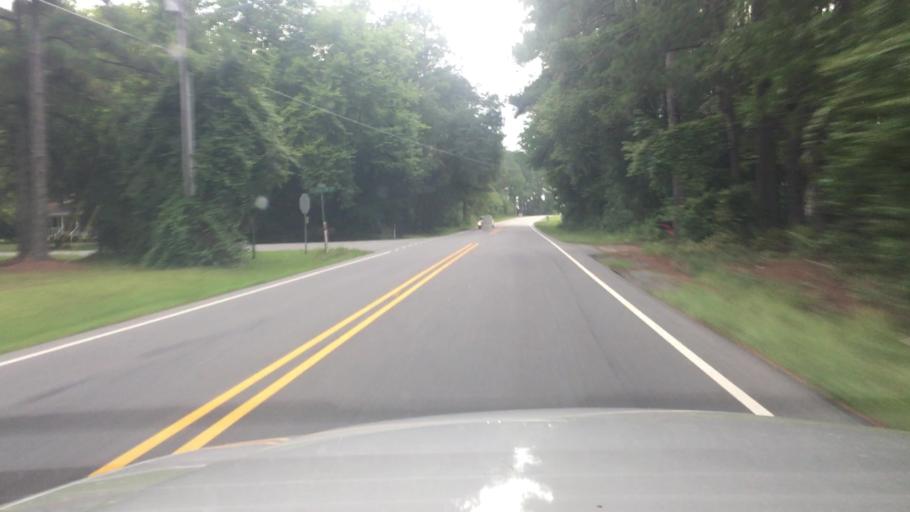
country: US
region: North Carolina
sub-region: Hoke County
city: Rockfish
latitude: 34.9645
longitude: -79.0270
